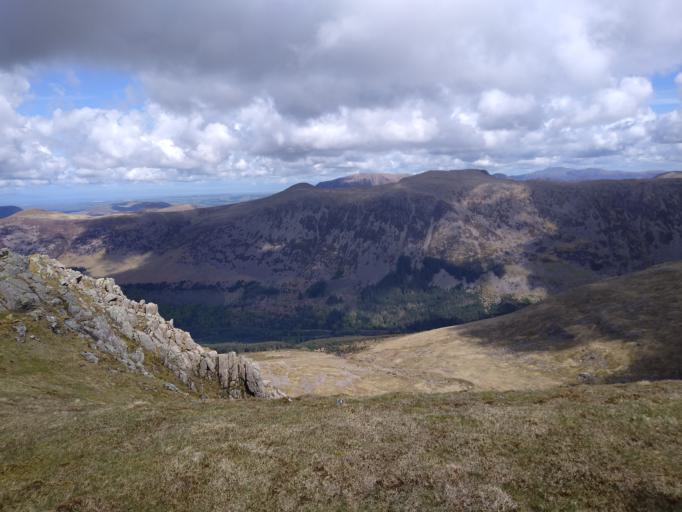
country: GB
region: England
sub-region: Cumbria
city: Cockermouth
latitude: 54.4943
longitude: -3.3031
